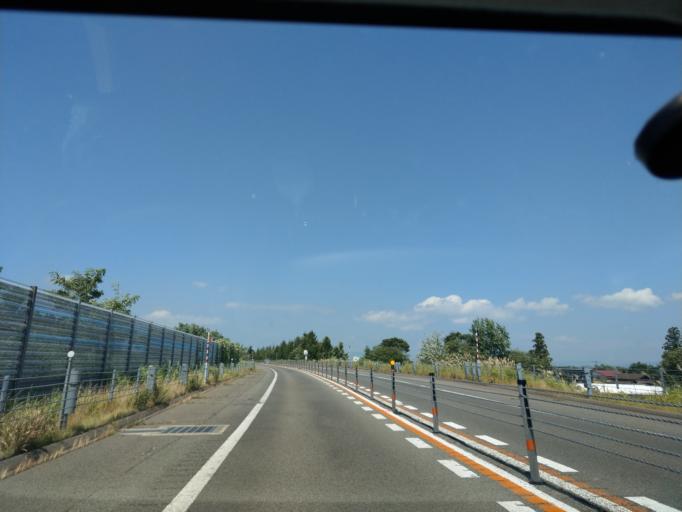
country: JP
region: Akita
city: Yokotemachi
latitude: 39.3417
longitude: 140.5008
